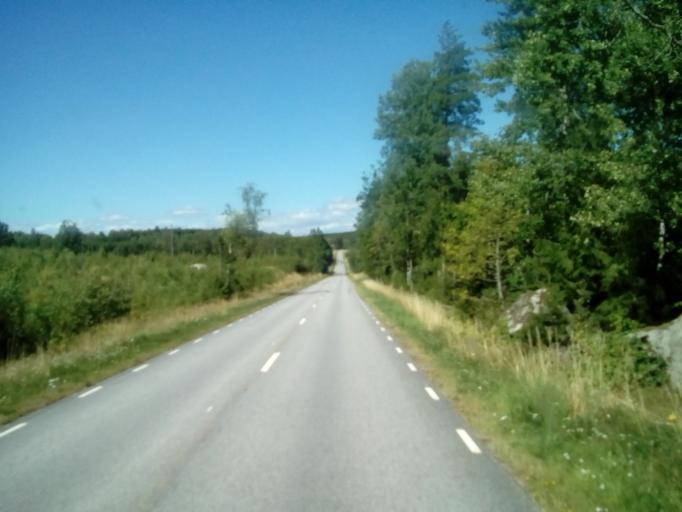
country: SE
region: Kalmar
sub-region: Vasterviks Kommun
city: Overum
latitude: 57.8996
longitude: 16.0606
